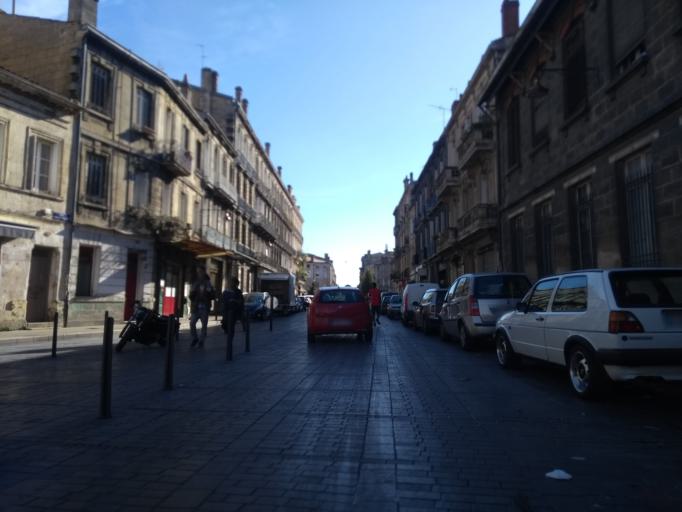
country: FR
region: Aquitaine
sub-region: Departement de la Gironde
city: Bordeaux
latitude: 44.8335
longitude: -0.5666
